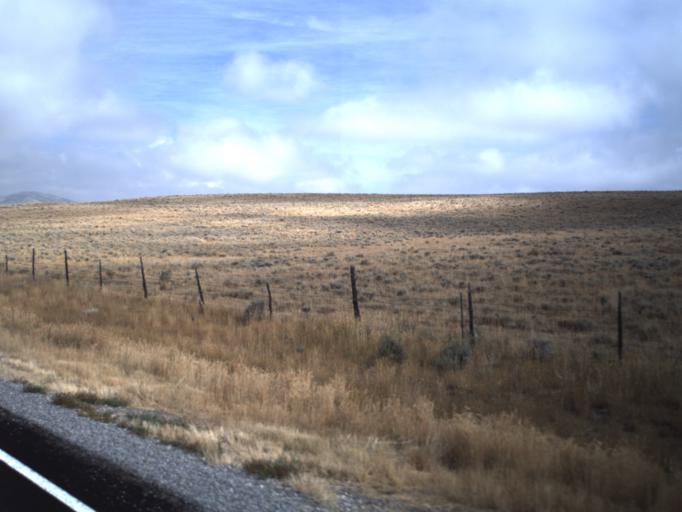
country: US
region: Utah
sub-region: Rich County
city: Randolph
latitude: 41.4864
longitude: -111.1176
